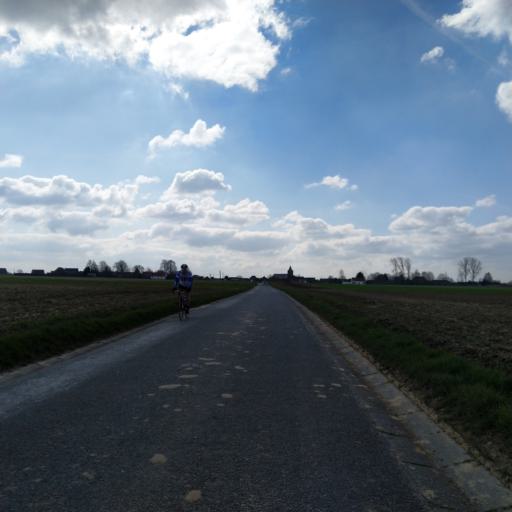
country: BE
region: Wallonia
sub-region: Province du Hainaut
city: Lens
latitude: 50.5708
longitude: 3.9409
